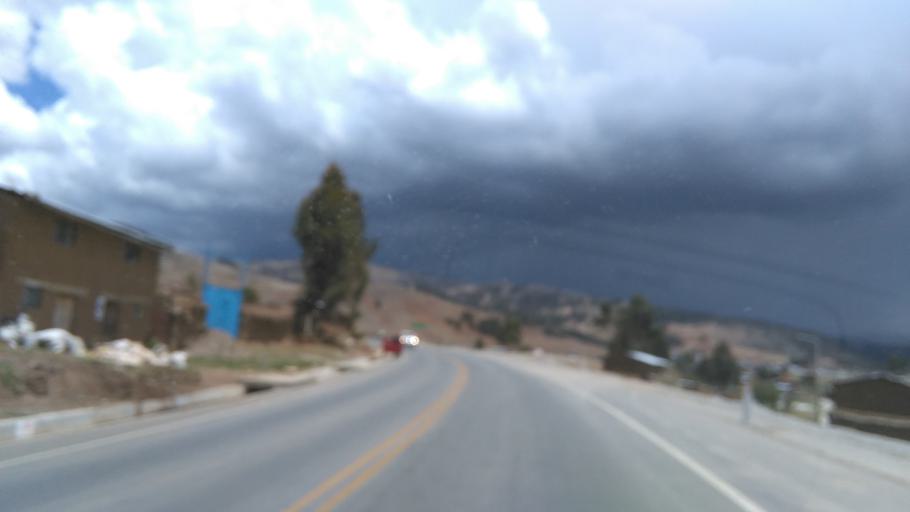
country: PE
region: Apurimac
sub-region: Provincia de Andahuaylas
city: San Jeronimo
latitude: -13.7012
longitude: -73.3548
